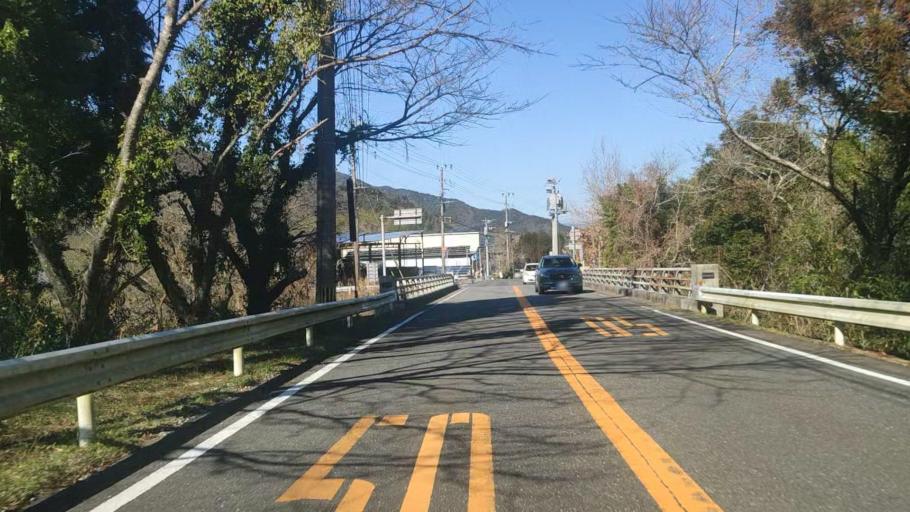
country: JP
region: Oita
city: Saiki
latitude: 32.9015
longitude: 131.9339
